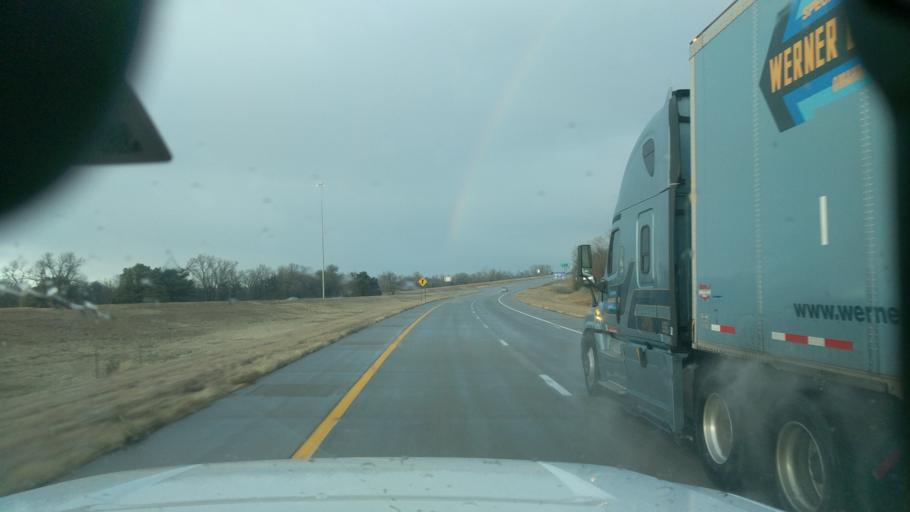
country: US
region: Kansas
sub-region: Harvey County
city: Newton
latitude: 38.0289
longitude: -97.3276
